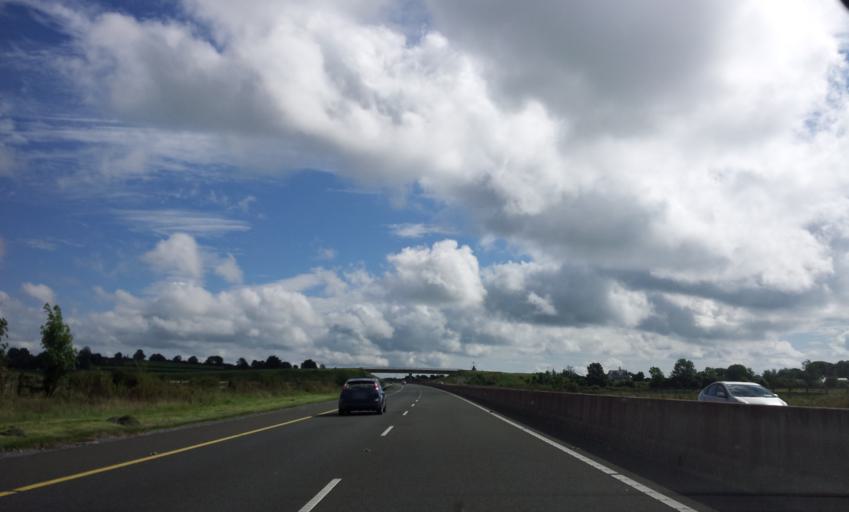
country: IE
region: Munster
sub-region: North Tipperary
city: Roscrea
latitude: 52.9147
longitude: -7.7026
